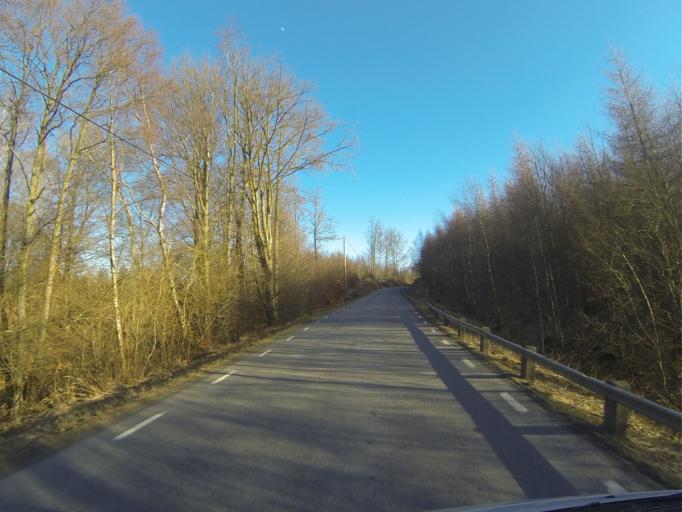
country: SE
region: Skane
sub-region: Horby Kommun
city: Hoerby
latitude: 55.9015
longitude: 13.6593
